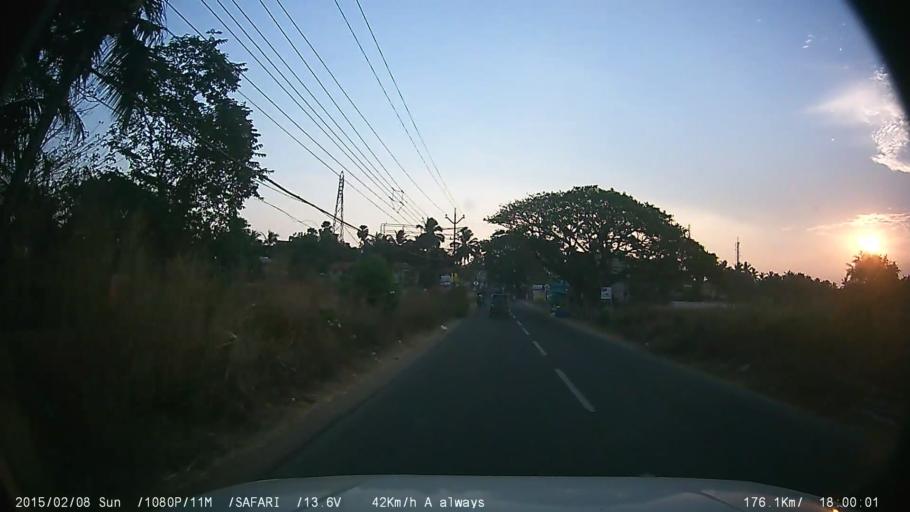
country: IN
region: Kerala
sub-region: Palakkad district
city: Palakkad
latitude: 10.7542
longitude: 76.6508
